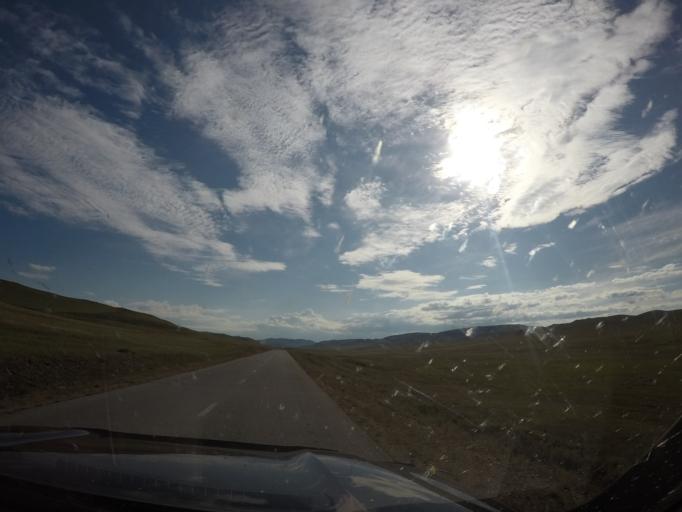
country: MN
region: Hentiy
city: Modot
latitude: 47.7508
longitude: 108.6201
